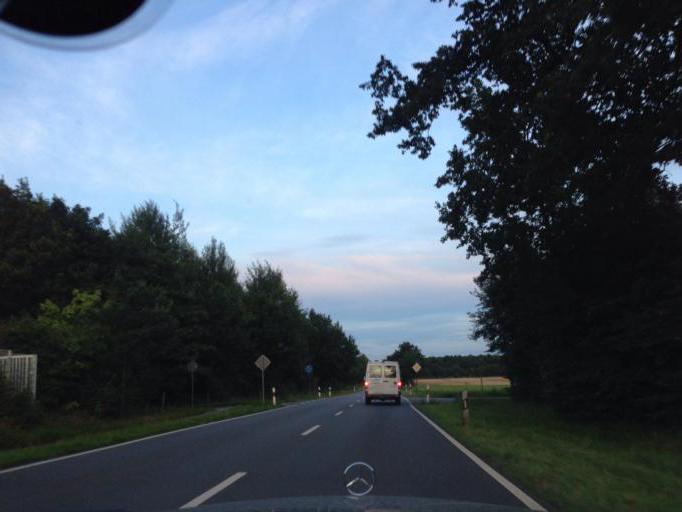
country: DE
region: Schleswig-Holstein
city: Bargteheide
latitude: 53.7186
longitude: 10.2813
